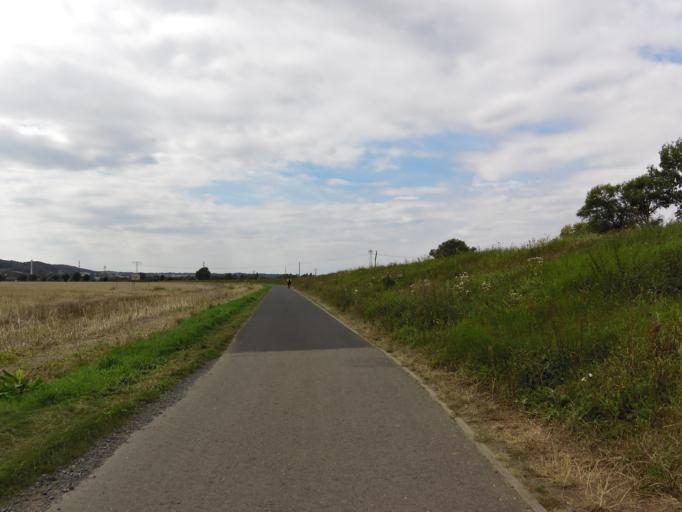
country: DE
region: Saxony
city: Radebeul
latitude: 51.0990
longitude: 13.6301
